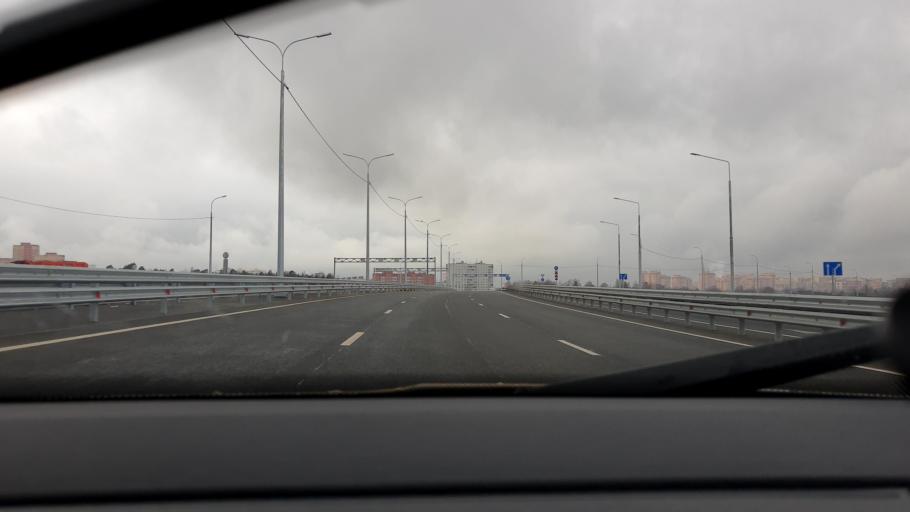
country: RU
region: Moskovskaya
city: Pushkino
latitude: 56.0116
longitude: 37.8834
